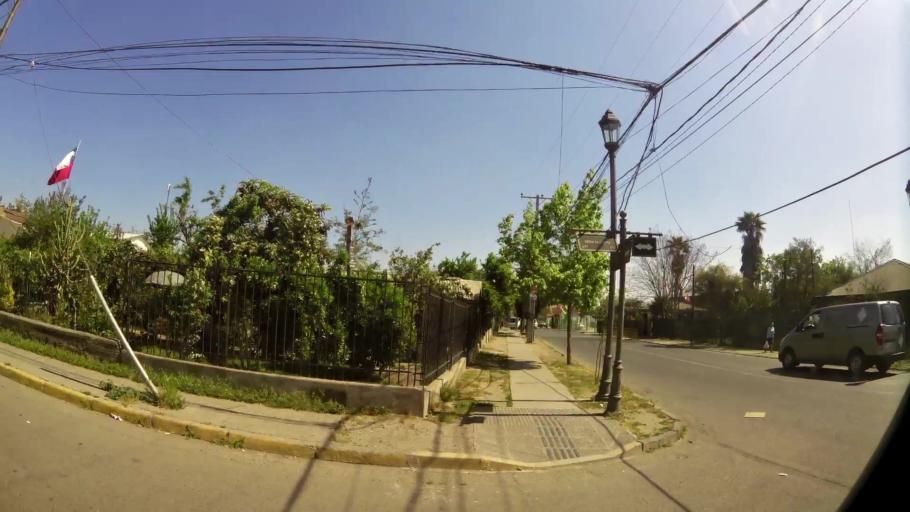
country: CL
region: Santiago Metropolitan
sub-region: Provincia de Talagante
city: Penaflor
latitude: -33.5699
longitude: -70.8044
